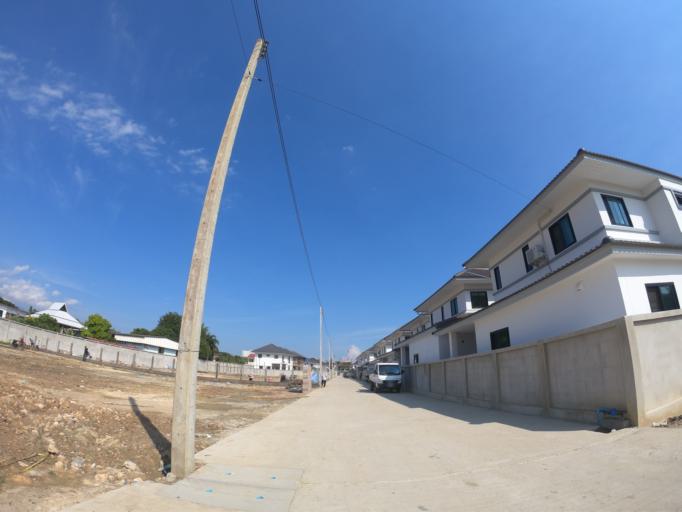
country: TH
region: Chiang Mai
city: Chiang Mai
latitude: 18.7520
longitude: 99.0058
